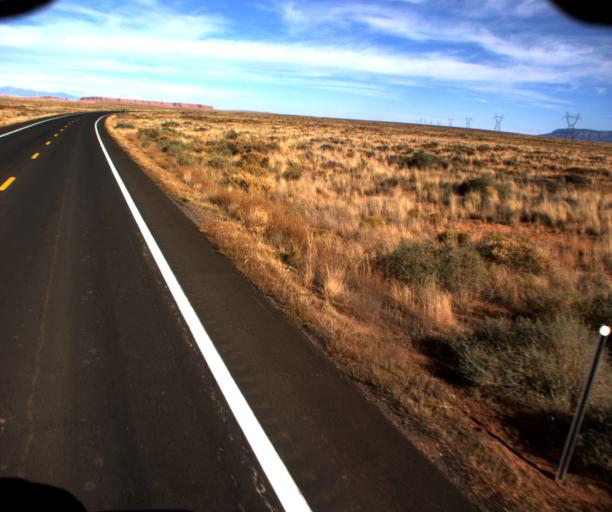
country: US
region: Arizona
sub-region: Apache County
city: Lukachukai
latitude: 36.9624
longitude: -109.4847
